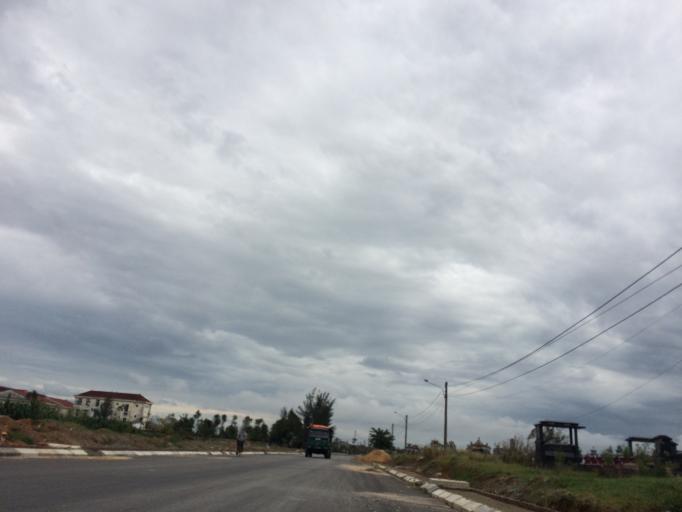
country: VN
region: Ha Tinh
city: Ha Tinh
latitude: 18.3618
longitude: 105.8929
